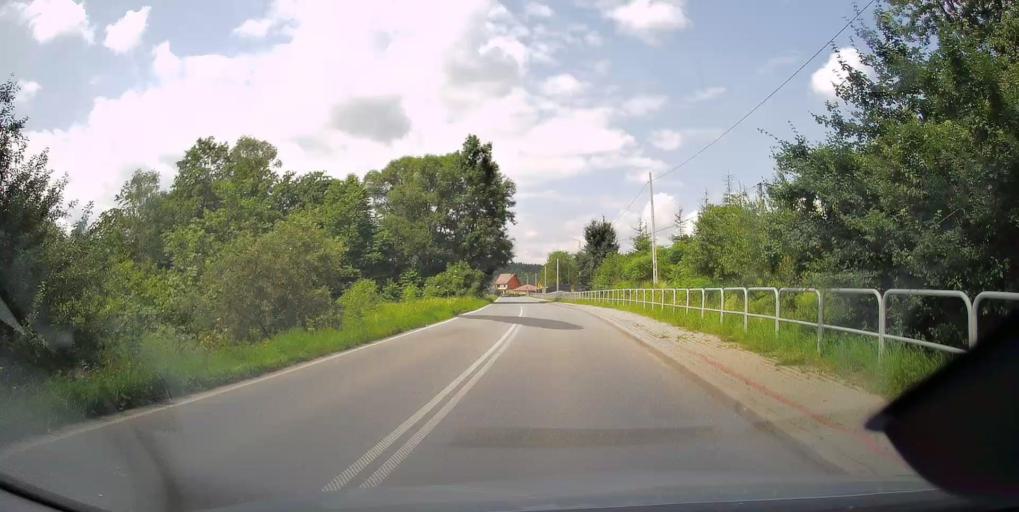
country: PL
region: Lesser Poland Voivodeship
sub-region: Powiat nowosadecki
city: Nowy Sacz
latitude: 49.6689
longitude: 20.7429
